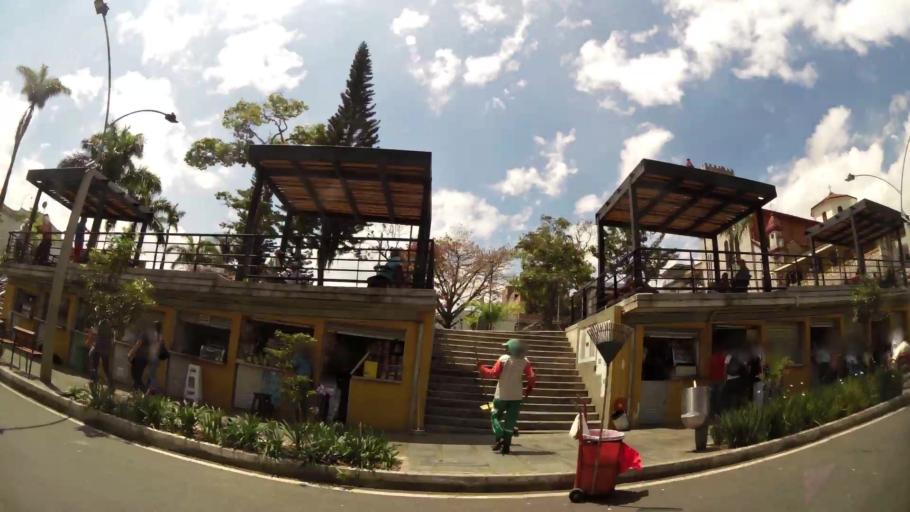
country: CO
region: Antioquia
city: La Estrella
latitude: 6.1849
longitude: -75.6566
